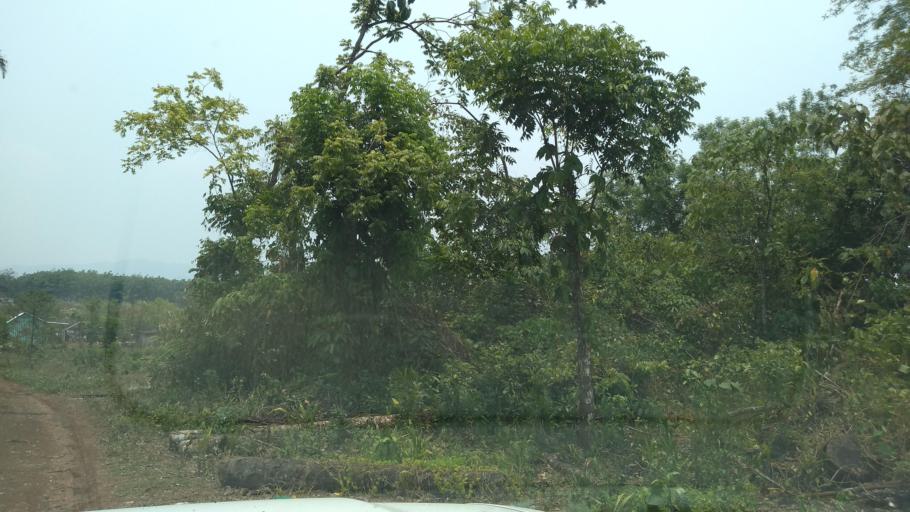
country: MX
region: Veracruz
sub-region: Tezonapa
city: Laguna Chica (Pueblo Nuevo)
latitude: 18.5131
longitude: -96.7574
